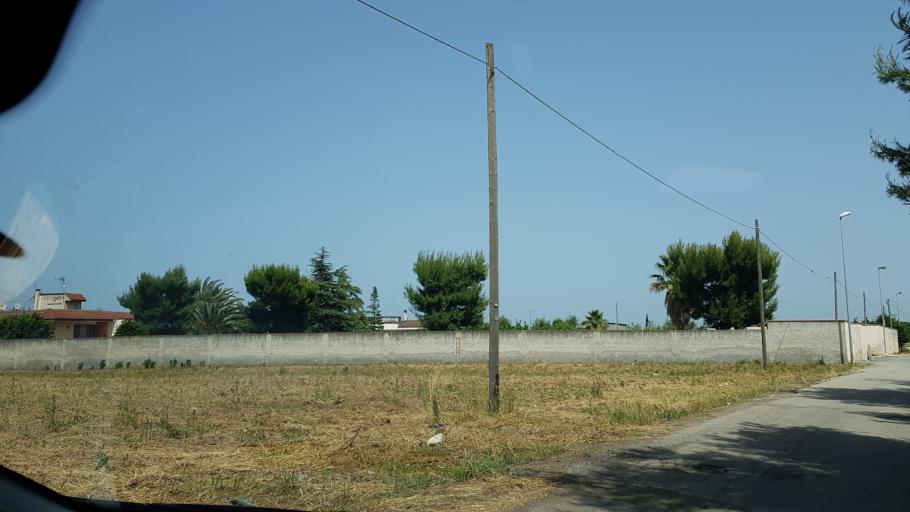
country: IT
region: Apulia
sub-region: Provincia di Brindisi
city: Mesagne
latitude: 40.5536
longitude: 17.8231
